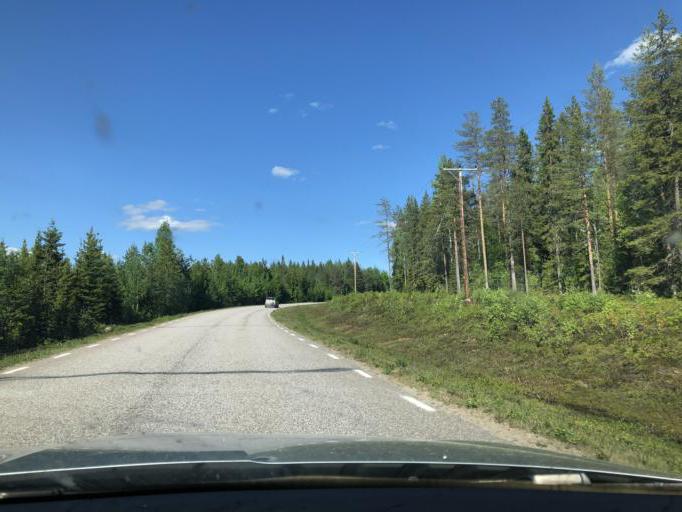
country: SE
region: Norrbotten
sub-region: Kalix Kommun
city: Kalix
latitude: 66.0183
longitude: 23.1448
